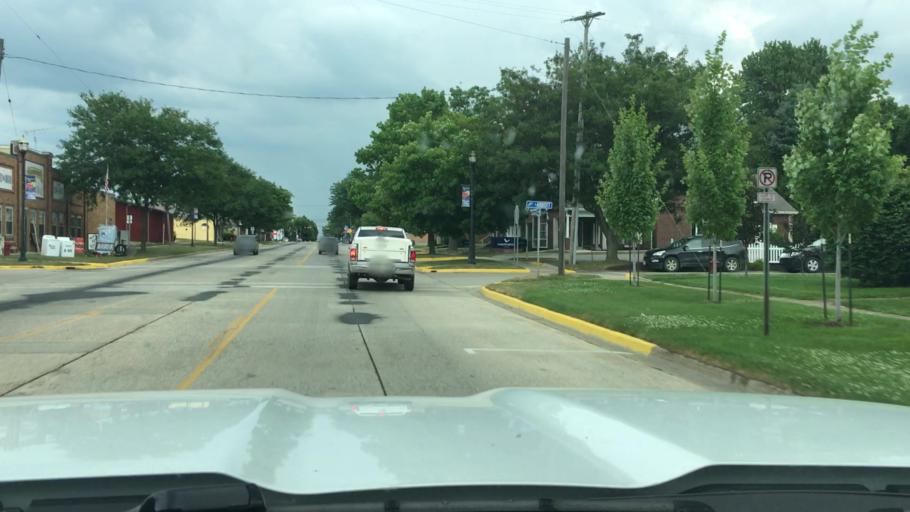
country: US
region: Michigan
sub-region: Montcalm County
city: Carson City
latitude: 43.1770
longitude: -84.8506
